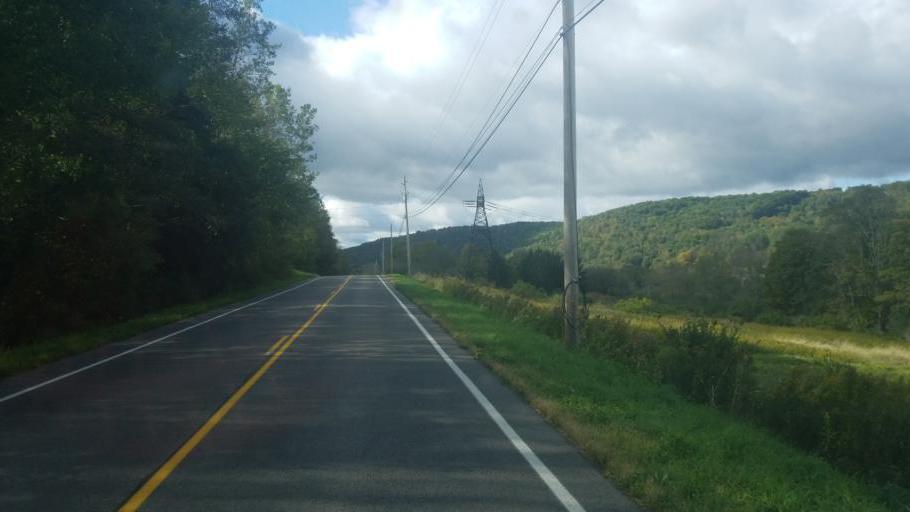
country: US
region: New York
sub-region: Cattaraugus County
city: Weston Mills
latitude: 42.1284
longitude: -78.3416
